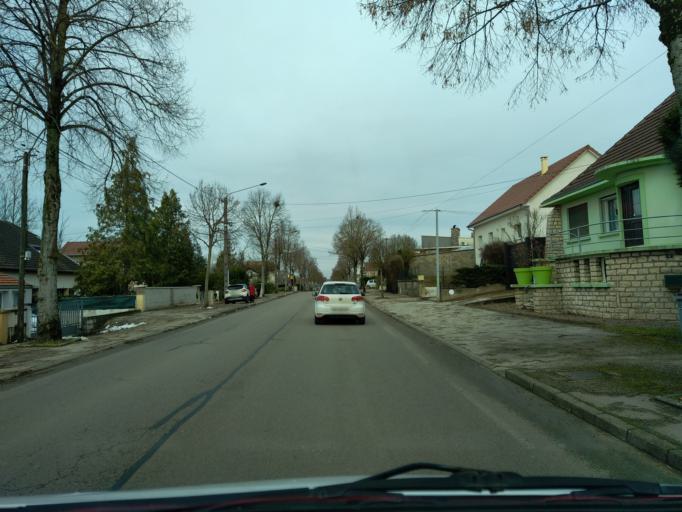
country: FR
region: Franche-Comte
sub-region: Departement de la Haute-Saone
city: Arc-les-Gray
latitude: 47.4639
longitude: 5.5832
